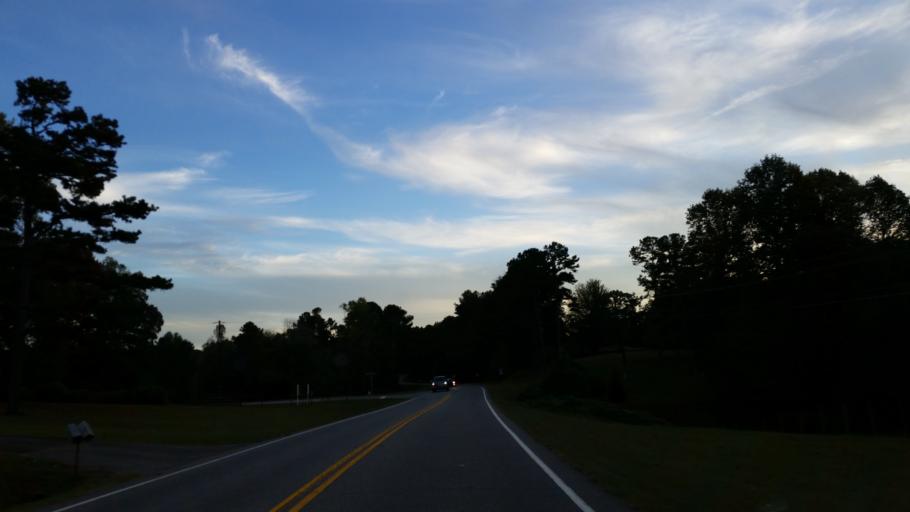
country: US
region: Georgia
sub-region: Dawson County
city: Dawsonville
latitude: 34.3974
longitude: -84.1229
